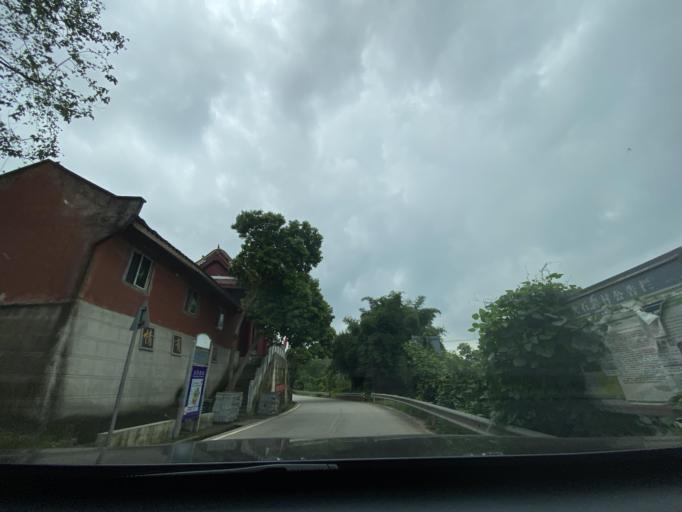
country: CN
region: Sichuan
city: Dongsheng
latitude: 30.4062
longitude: 104.0084
